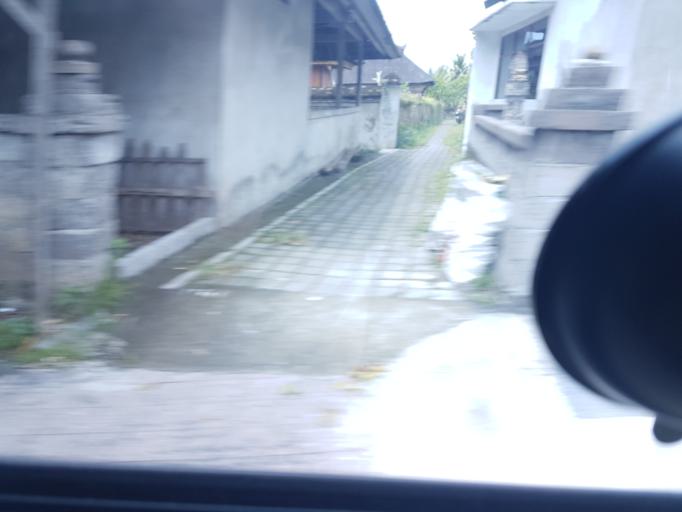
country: ID
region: Bali
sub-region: Kabupaten Gianyar
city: Ubud
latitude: -8.5119
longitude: 115.2935
